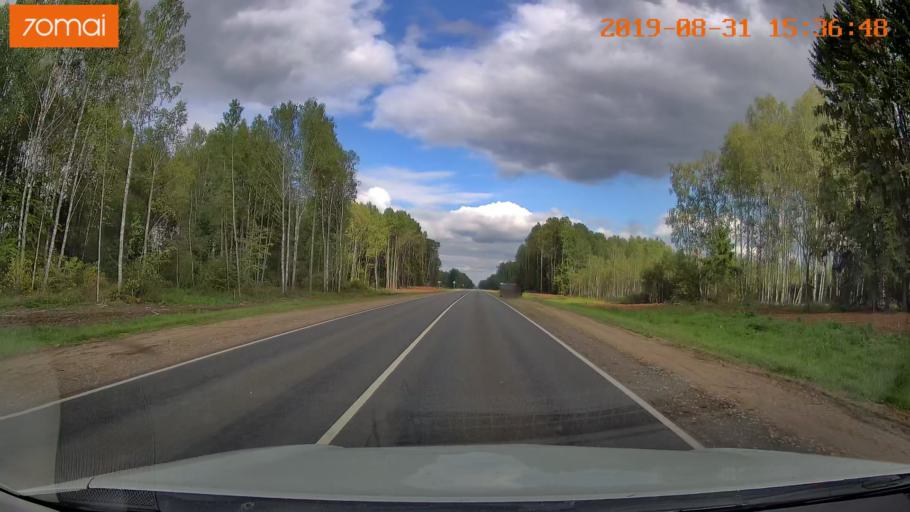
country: RU
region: Kaluga
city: Mosal'sk
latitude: 54.6137
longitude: 34.7678
